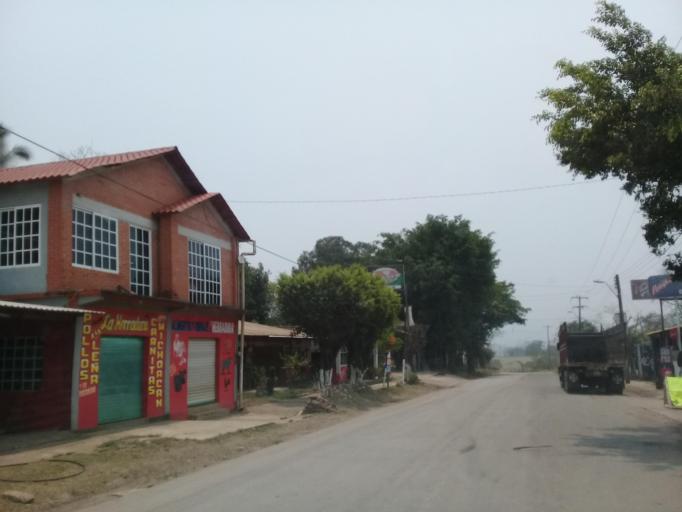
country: MX
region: Veracruz
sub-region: Tezonapa
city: Laguna Chica (Pueblo Nuevo)
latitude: 18.5432
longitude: -96.7364
